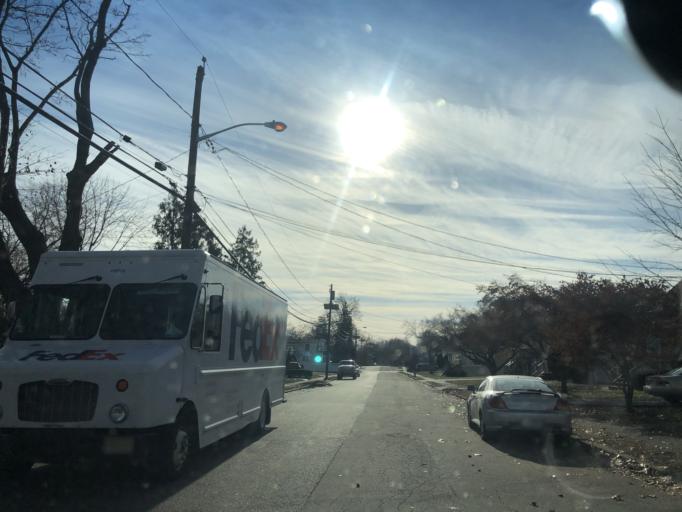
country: US
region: New Jersey
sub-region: Bergen County
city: Fair Lawn
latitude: 40.9281
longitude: -74.1366
